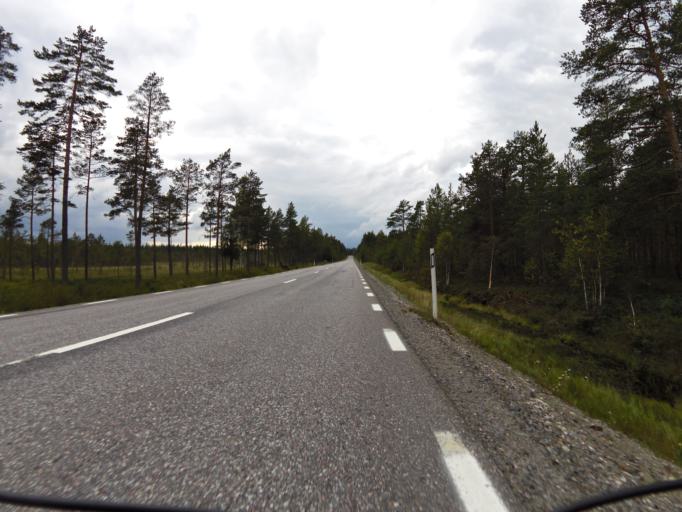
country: SE
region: Gaevleborg
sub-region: Gavle Kommun
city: Norrsundet
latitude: 60.8975
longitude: 16.9405
